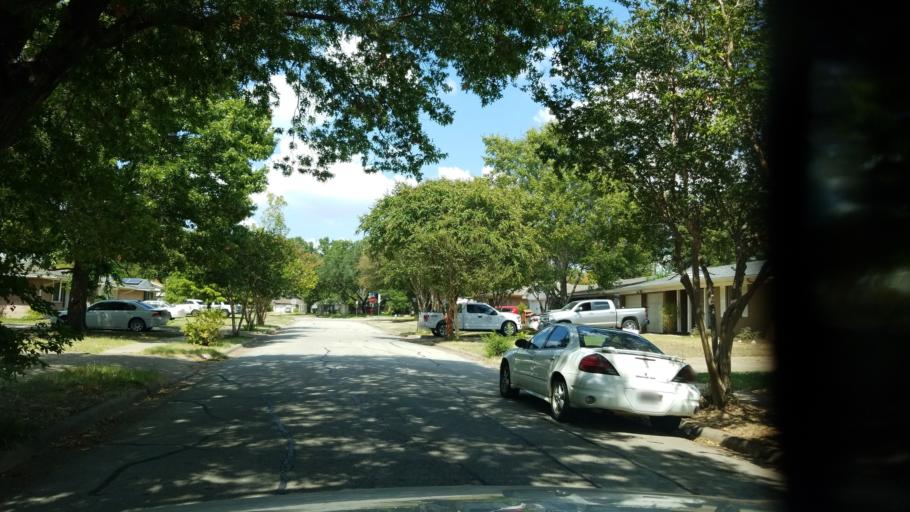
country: US
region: Texas
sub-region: Dallas County
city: Richardson
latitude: 32.9558
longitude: -96.7650
